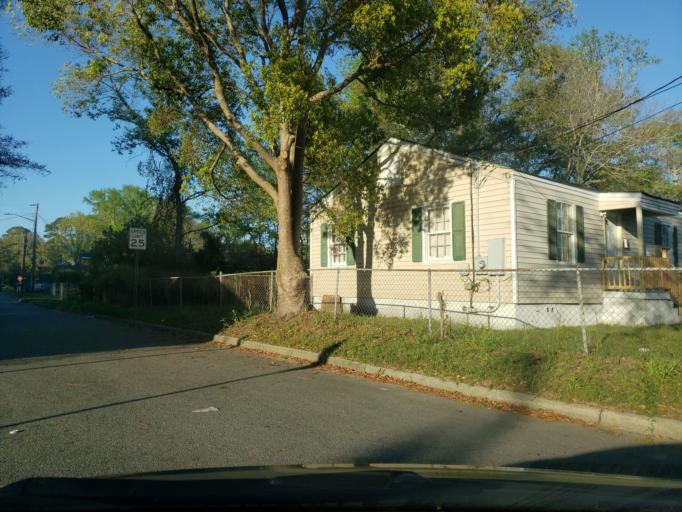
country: US
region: Georgia
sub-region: Chatham County
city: Thunderbolt
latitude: 32.0542
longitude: -81.0585
